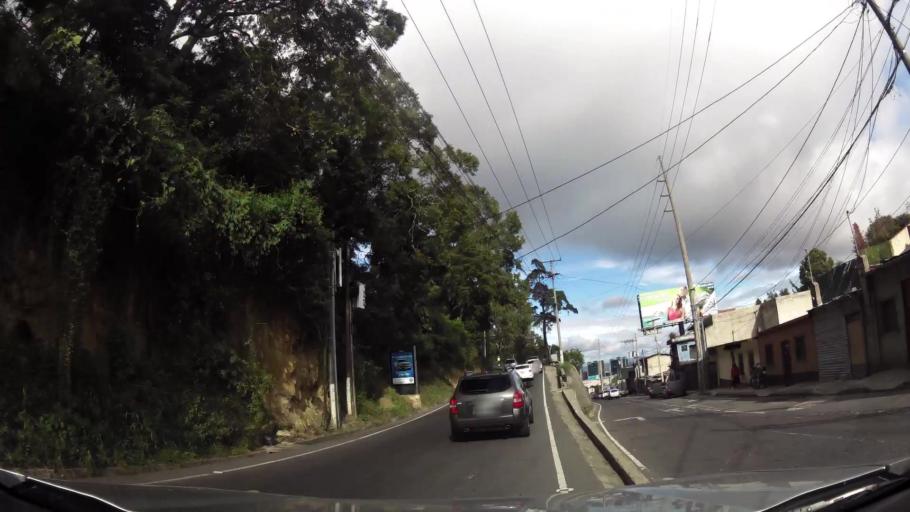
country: GT
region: Guatemala
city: Santa Catarina Pinula
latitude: 14.5721
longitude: -90.4883
